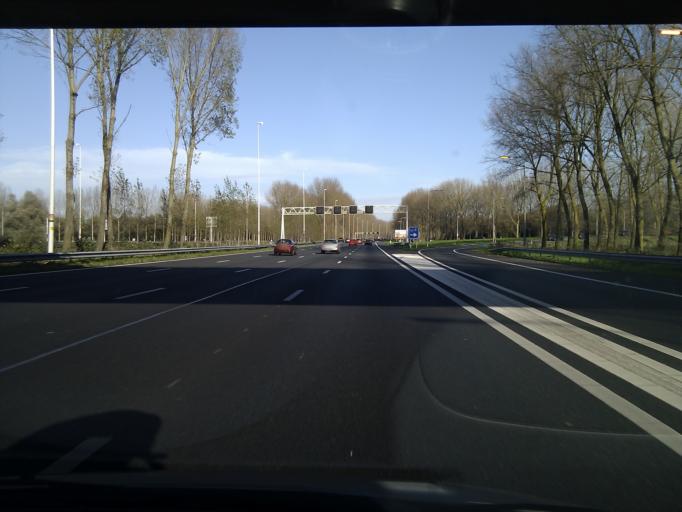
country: NL
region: South Holland
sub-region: Bodegraven-Reeuwijk
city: Reeuwijk
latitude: 52.0571
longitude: 4.7273
